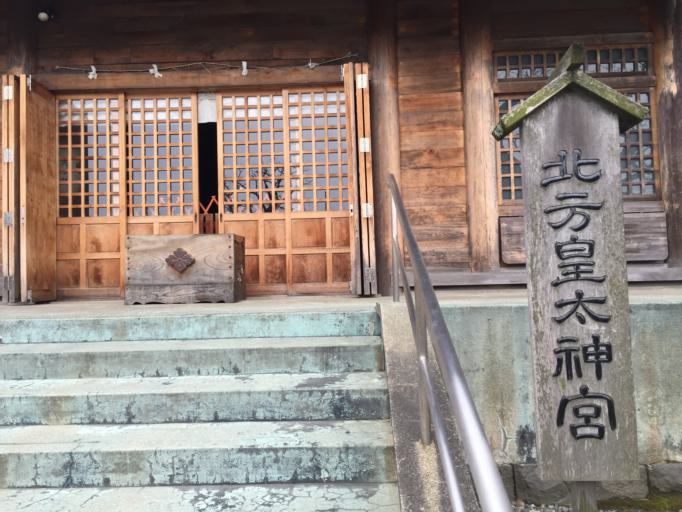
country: JP
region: Kanagawa
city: Yokohama
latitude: 35.4315
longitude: 139.6535
